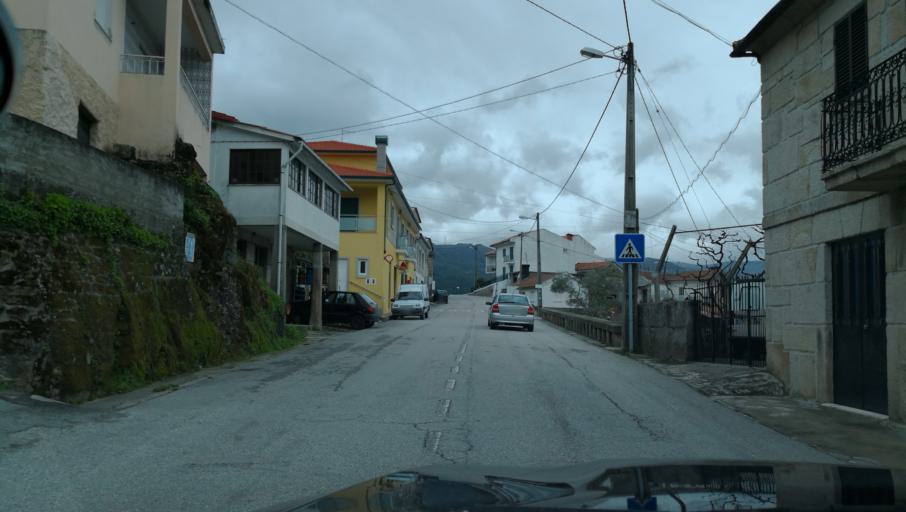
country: PT
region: Vila Real
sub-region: Vila Real
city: Vila Real
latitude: 41.2778
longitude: -7.7787
